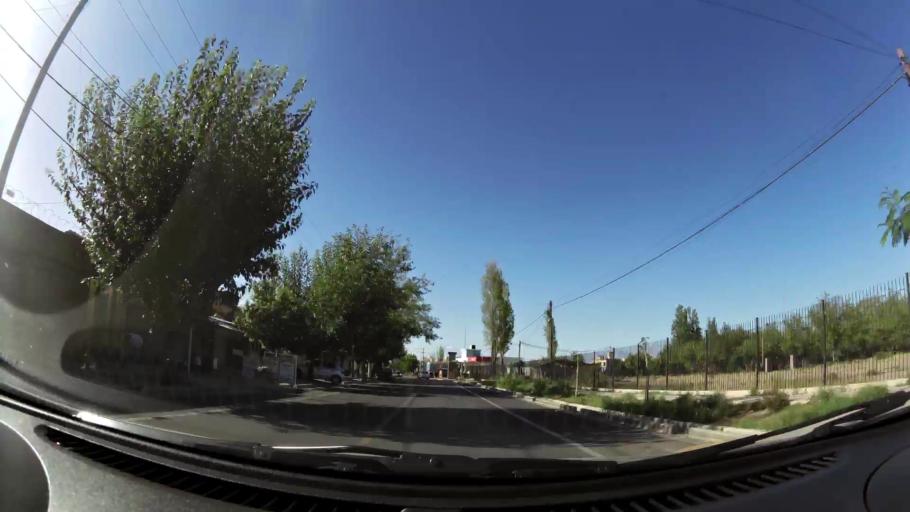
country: AR
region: Mendoza
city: Villa Nueva
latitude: -32.9138
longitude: -68.7979
